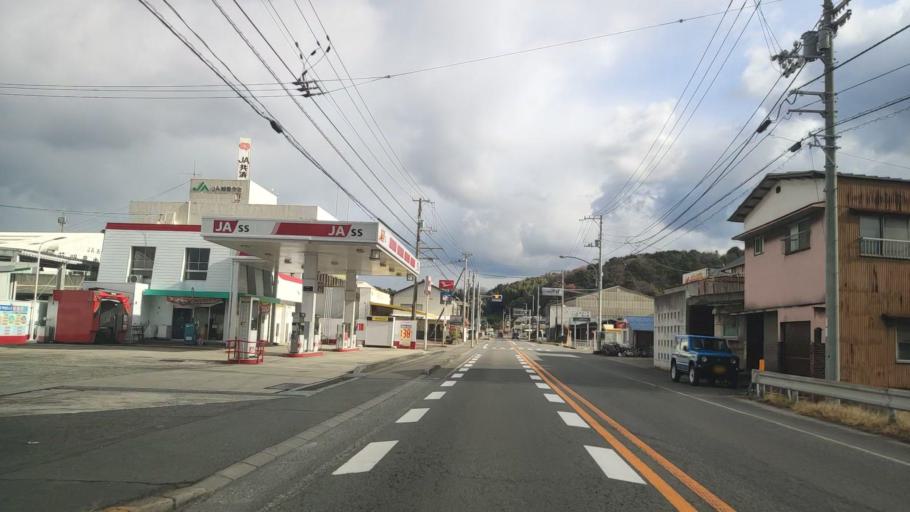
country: JP
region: Ehime
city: Hojo
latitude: 34.0380
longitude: 132.8437
